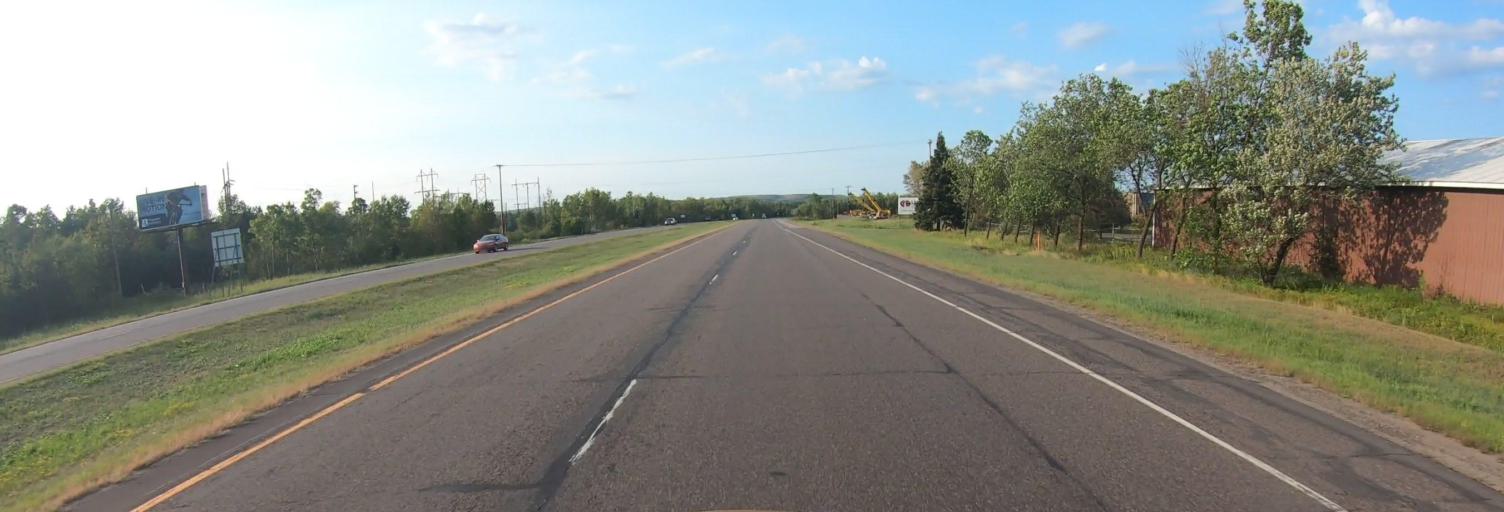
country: US
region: Minnesota
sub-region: Saint Louis County
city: Parkville
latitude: 47.5236
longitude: -92.5625
